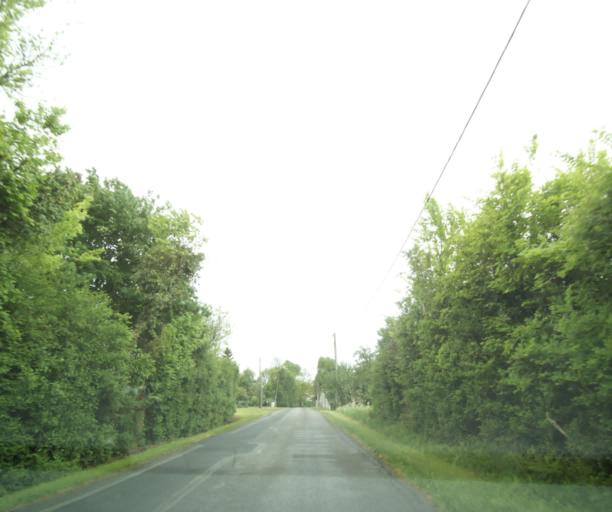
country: FR
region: Poitou-Charentes
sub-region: Departement de la Charente-Maritime
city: Chaniers
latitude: 45.6926
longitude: -0.5054
